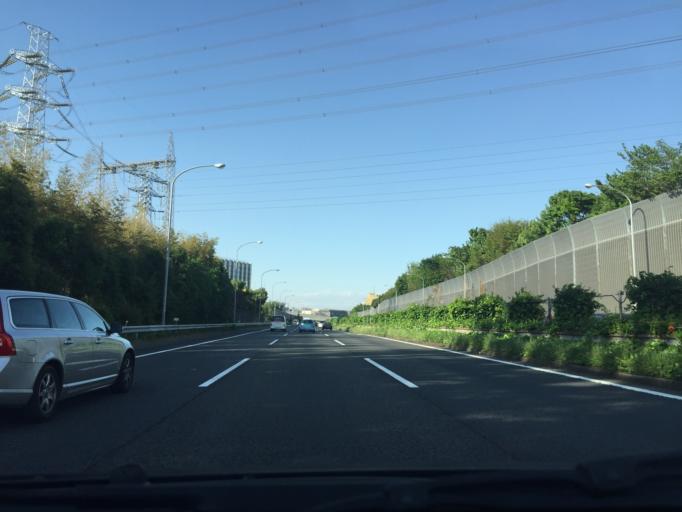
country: JP
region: Tokyo
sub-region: Machida-shi
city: Machida
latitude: 35.5538
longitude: 139.5490
